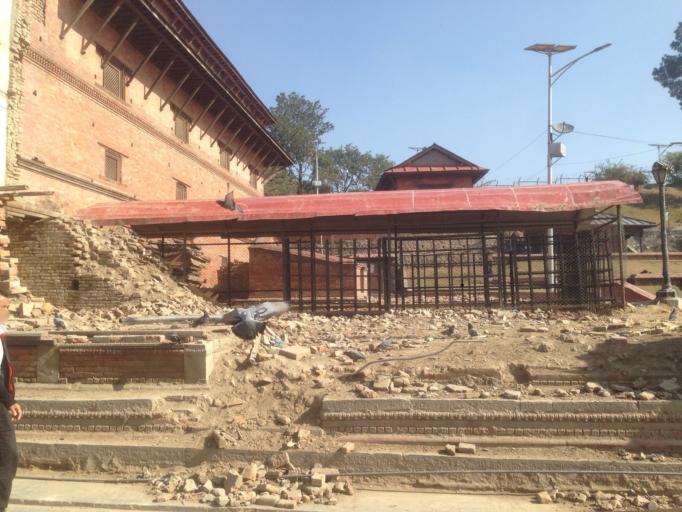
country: NP
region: Central Region
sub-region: Bagmati Zone
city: Kathmandu
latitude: 27.7107
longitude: 85.3475
